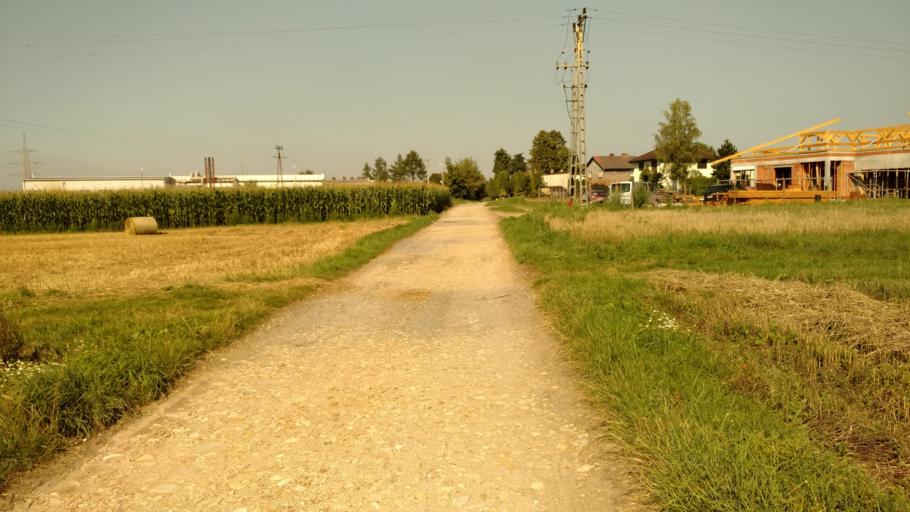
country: PL
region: Silesian Voivodeship
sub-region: Powiat pszczynski
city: Jankowice
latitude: 49.9968
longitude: 18.9874
